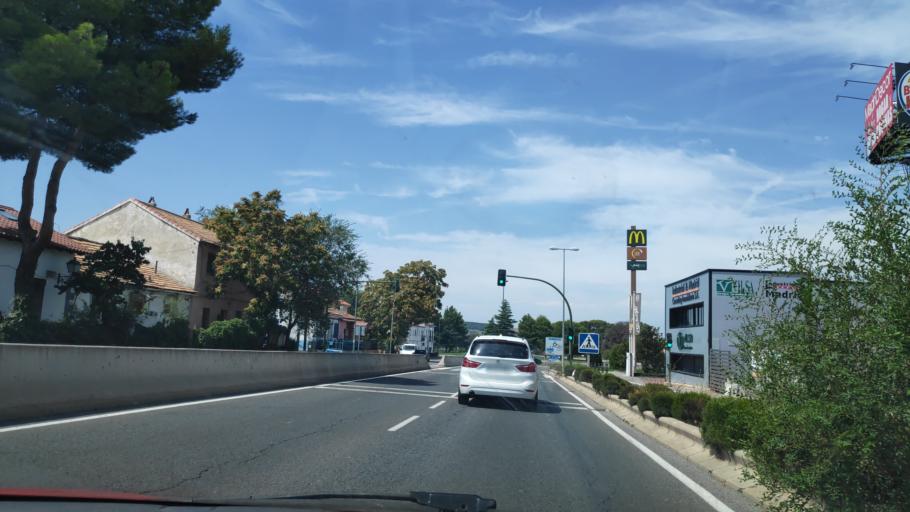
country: ES
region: Madrid
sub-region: Provincia de Madrid
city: Vaciamadrid
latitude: 40.3116
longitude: -3.4864
